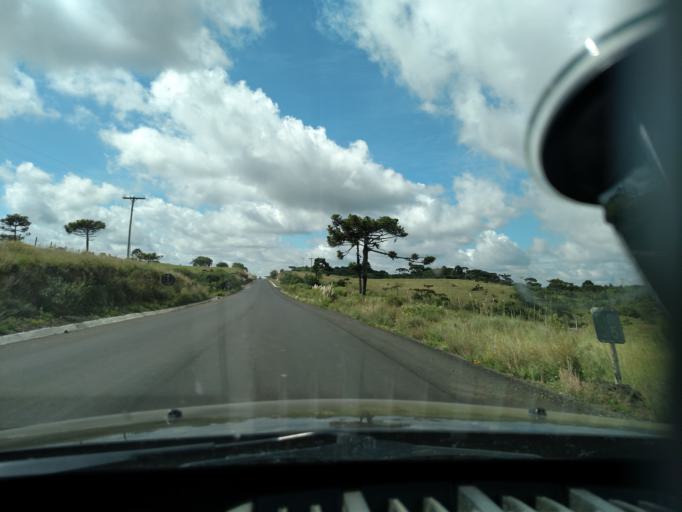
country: BR
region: Santa Catarina
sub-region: Sao Joaquim
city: Sao Joaquim
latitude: -28.0183
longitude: -50.0838
